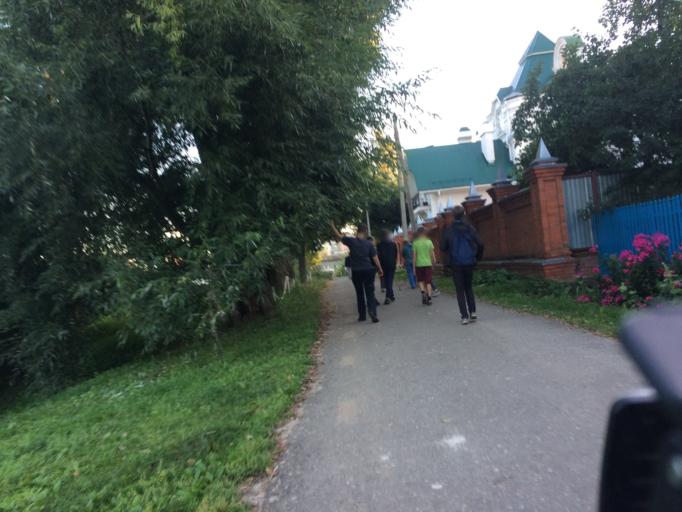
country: RU
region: Mariy-El
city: Yoshkar-Ola
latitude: 56.6400
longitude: 47.9053
